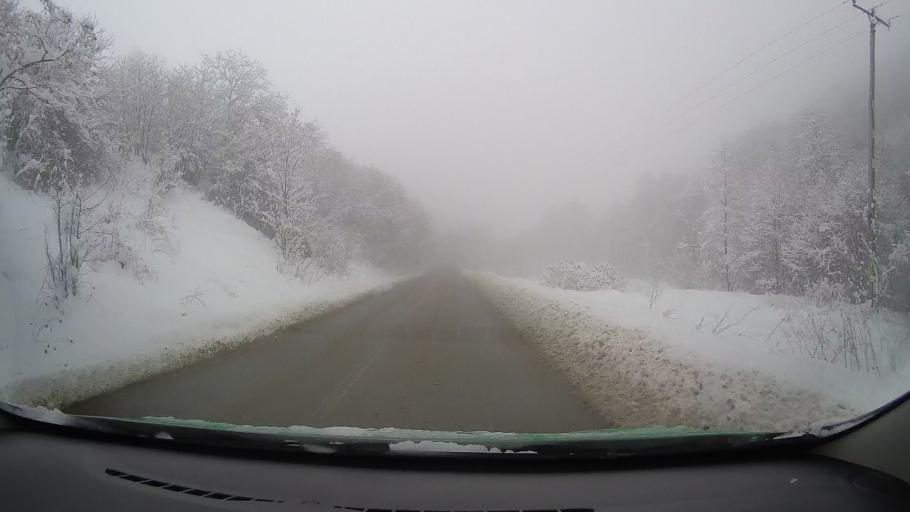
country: RO
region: Sibiu
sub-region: Comuna Poiana Sibiului
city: Poiana Sibiului
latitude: 45.8083
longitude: 23.7671
